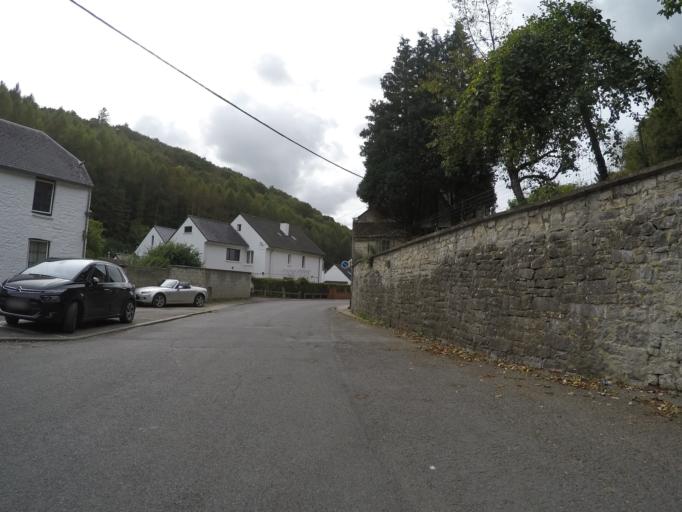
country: BE
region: Wallonia
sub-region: Province de Namur
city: Dinant
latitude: 50.2702
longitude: 4.9149
